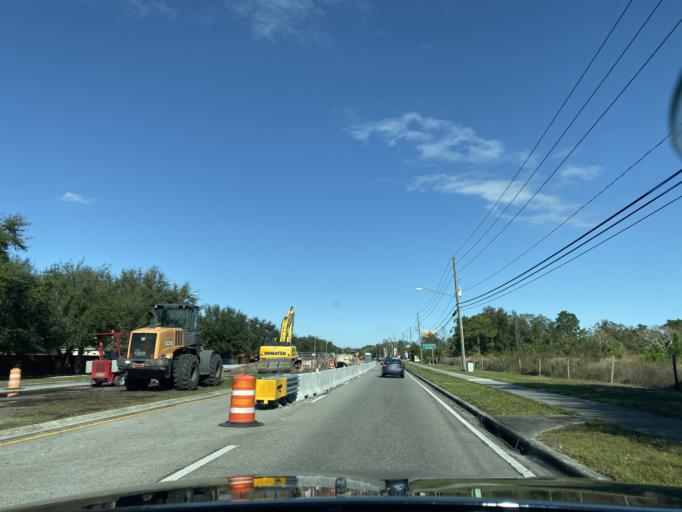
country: US
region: Florida
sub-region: Orange County
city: Alafaya
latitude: 28.5942
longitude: -81.2447
